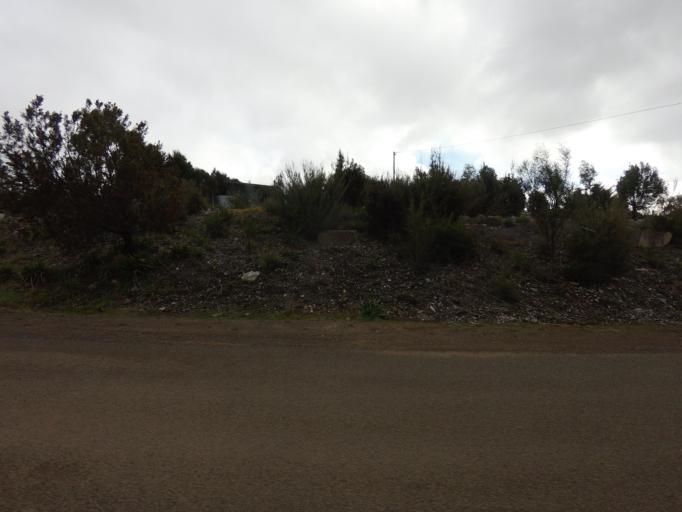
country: AU
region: Tasmania
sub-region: Sorell
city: Sorell
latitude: -42.5350
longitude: 147.9120
